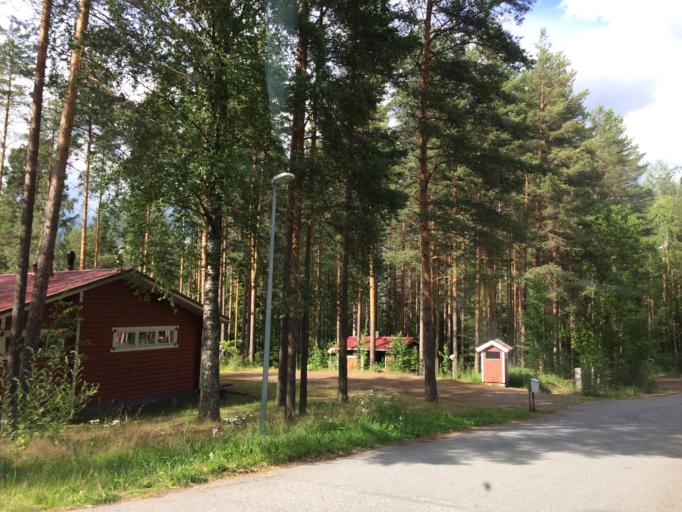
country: FI
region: Haeme
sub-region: Haemeenlinna
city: Turenki
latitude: 60.9408
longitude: 24.6403
